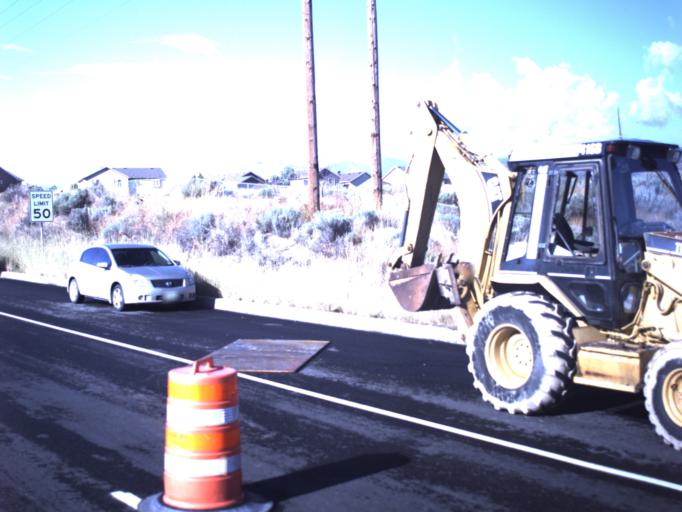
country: US
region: Utah
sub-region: Salt Lake County
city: Oquirrh
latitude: 40.6089
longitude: -112.0557
